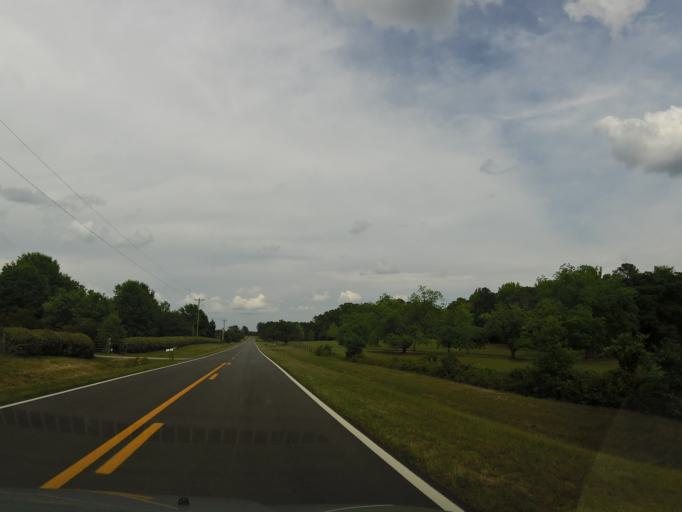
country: US
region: Georgia
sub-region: McDuffie County
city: Thomson
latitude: 33.5223
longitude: -82.4539
